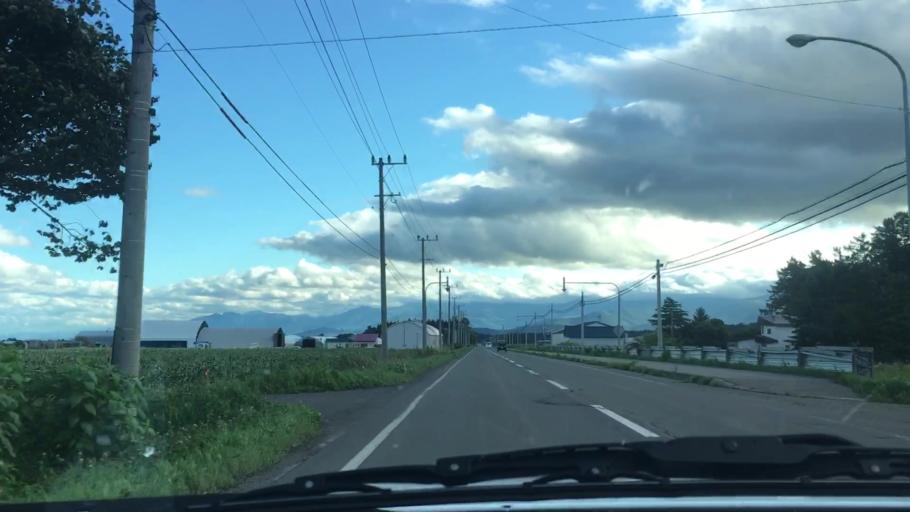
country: JP
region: Hokkaido
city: Otofuke
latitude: 43.1489
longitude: 142.8993
